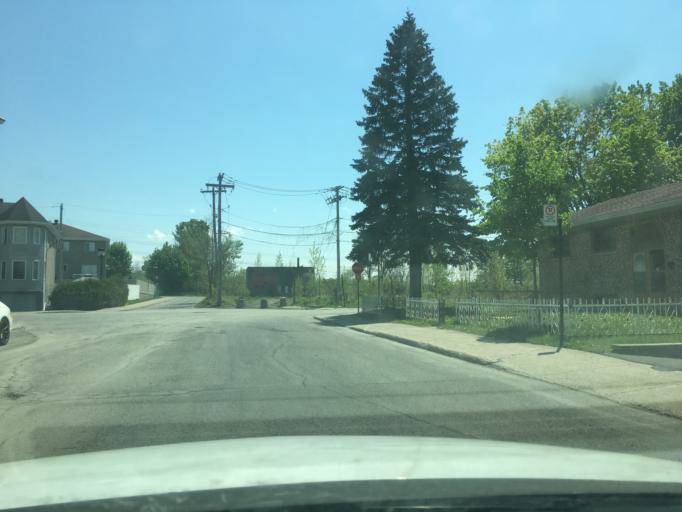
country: CA
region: Quebec
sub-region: Montreal
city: Saint-Leonard
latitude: 45.6254
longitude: -73.5899
